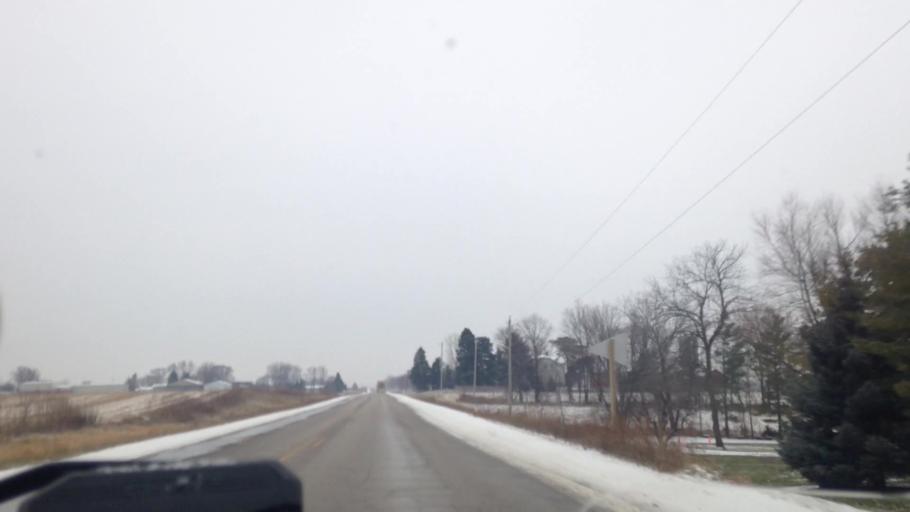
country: US
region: Wisconsin
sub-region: Dodge County
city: Mayville
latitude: 43.4261
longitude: -88.5422
